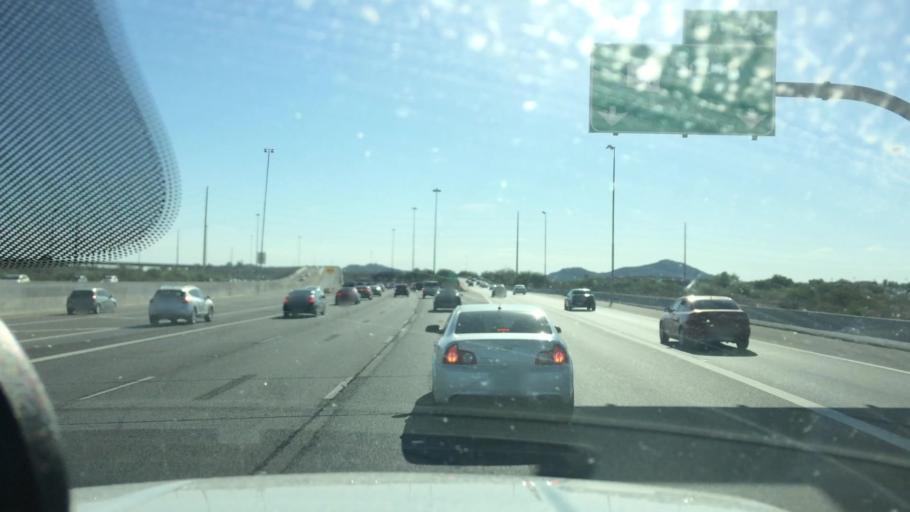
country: US
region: Arizona
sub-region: Maricopa County
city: Paradise Valley
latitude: 33.6738
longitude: -111.9900
